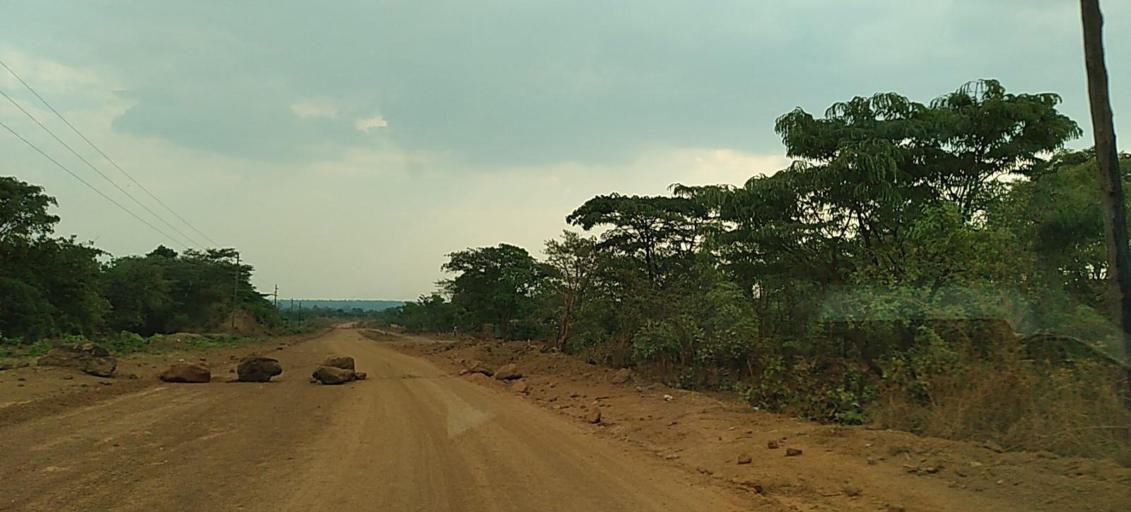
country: ZM
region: Copperbelt
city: Kalulushi
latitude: -12.9228
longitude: 27.9408
